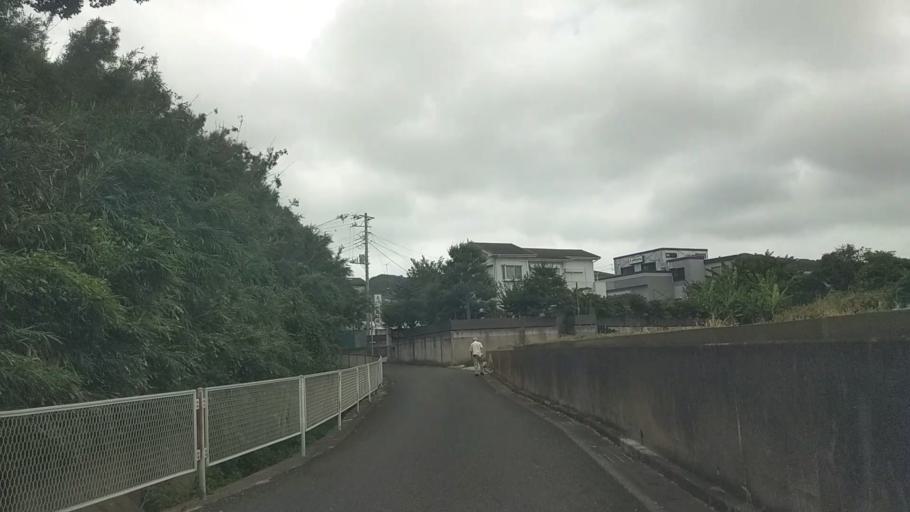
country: JP
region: Kanagawa
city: Hayama
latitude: 35.2299
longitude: 139.6240
